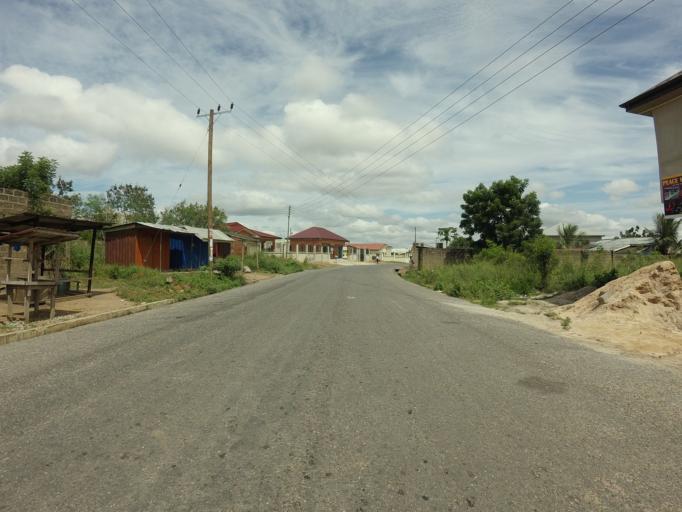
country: GH
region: Central
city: Kasoa
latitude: 5.5238
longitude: -0.4500
